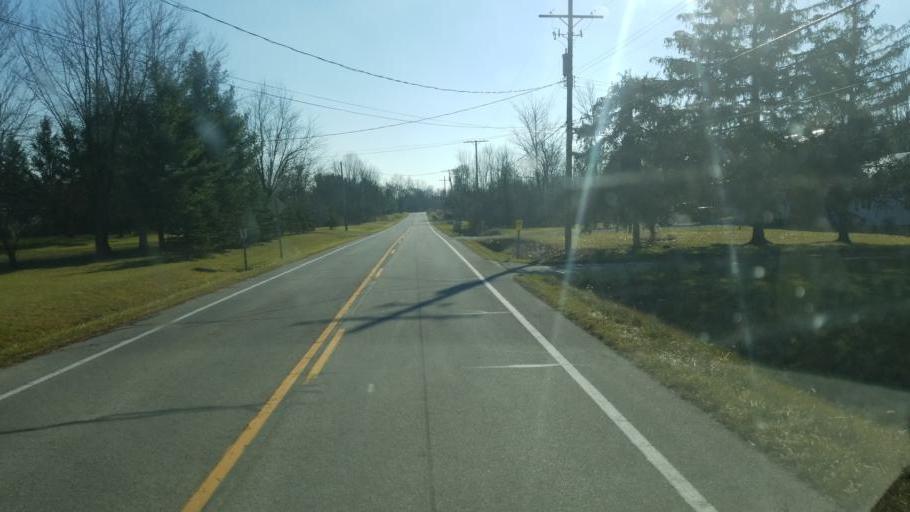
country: US
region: Ohio
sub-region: Geauga County
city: Burton
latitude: 41.4796
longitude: -81.2173
